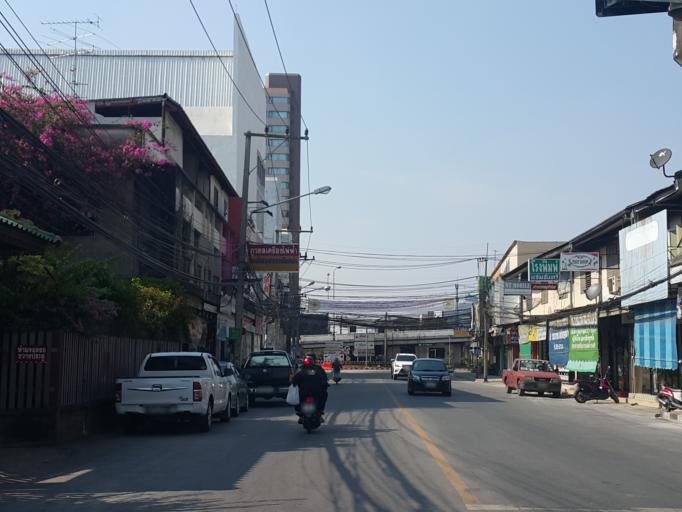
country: TH
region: Phitsanulok
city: Phitsanulok
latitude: 16.8198
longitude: 100.2651
